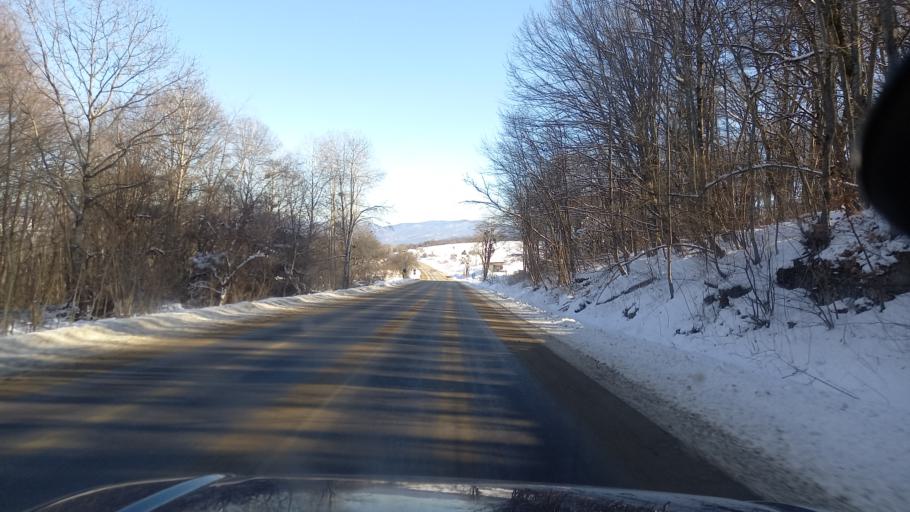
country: RU
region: Adygeya
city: Kamennomostskiy
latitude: 44.2319
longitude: 40.1247
